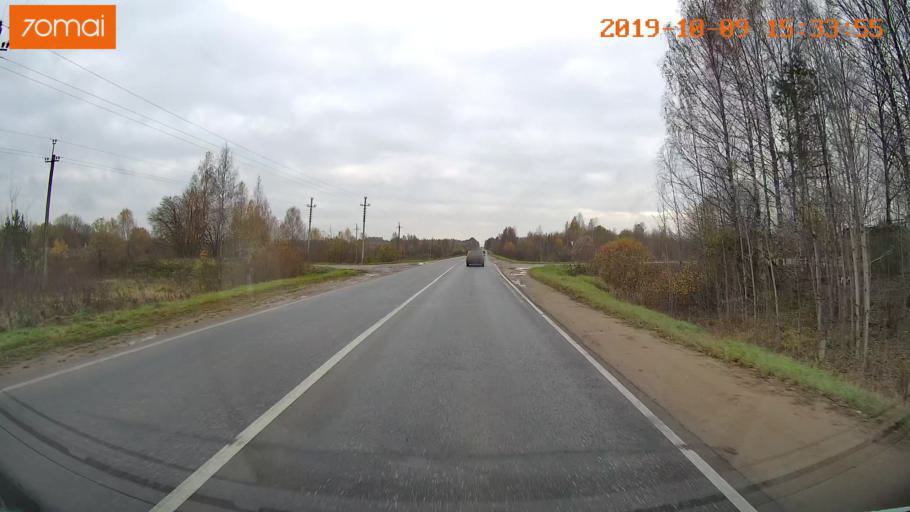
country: RU
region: Kostroma
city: Oktyabr'skiy
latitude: 57.9458
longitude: 41.2549
